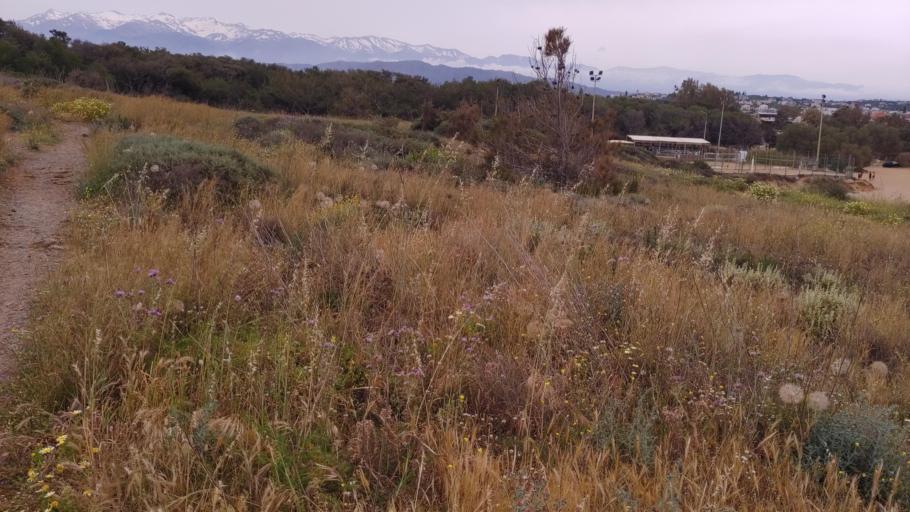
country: GR
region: Crete
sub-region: Nomos Chanias
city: Daratsos
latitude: 35.5151
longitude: 23.9803
